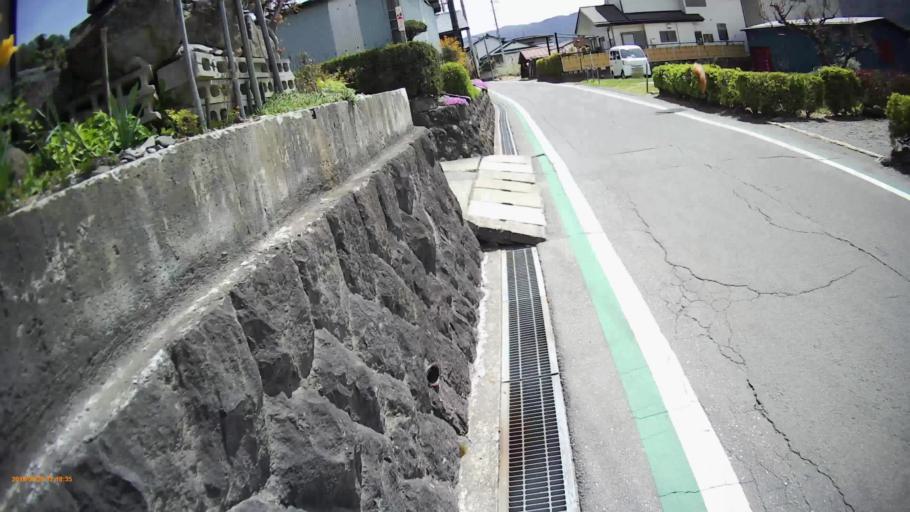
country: JP
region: Nagano
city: Chino
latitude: 36.0166
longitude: 138.1380
